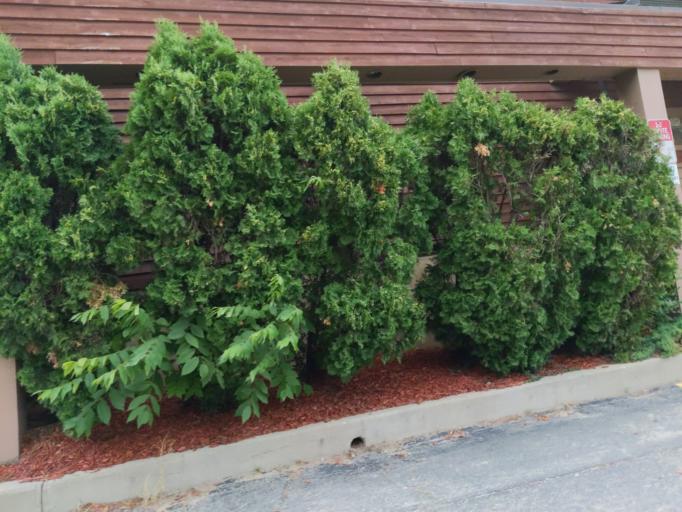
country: US
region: Michigan
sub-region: Livingston County
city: Brighton
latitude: 42.4628
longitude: -83.8478
